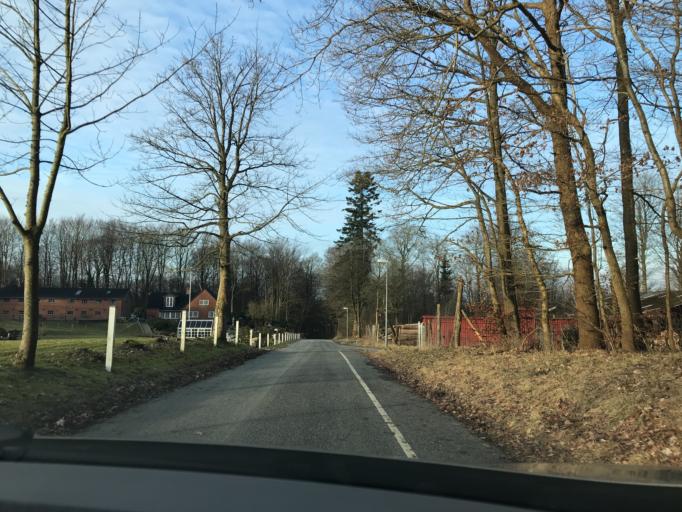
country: DK
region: South Denmark
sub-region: Vejle Kommune
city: Vejle
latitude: 55.6883
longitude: 9.5312
